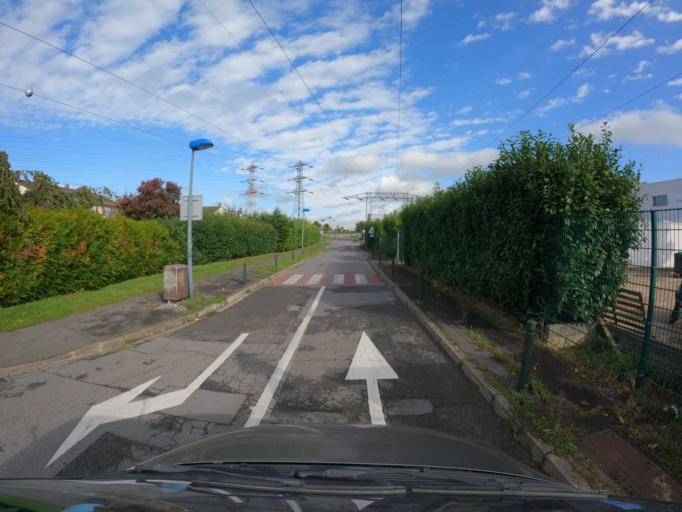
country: FR
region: Ile-de-France
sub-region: Departement de Seine-et-Marne
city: Brou-sur-Chantereine
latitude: 48.8869
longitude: 2.6135
